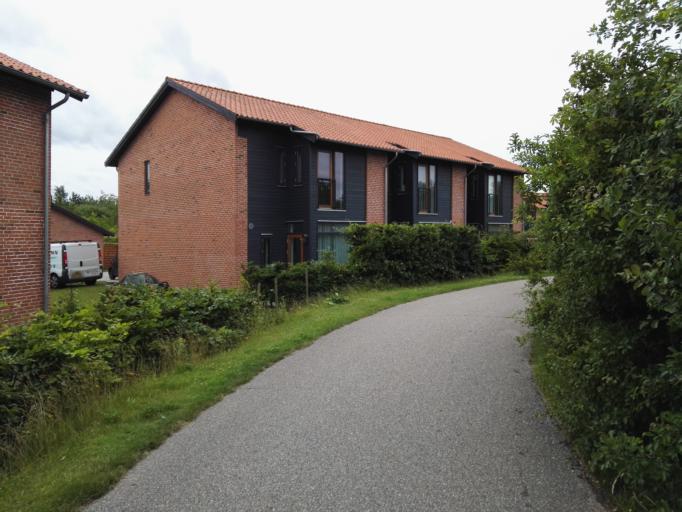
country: DK
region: Capital Region
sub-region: Egedal Kommune
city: Olstykke
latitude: 55.7720
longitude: 12.1695
